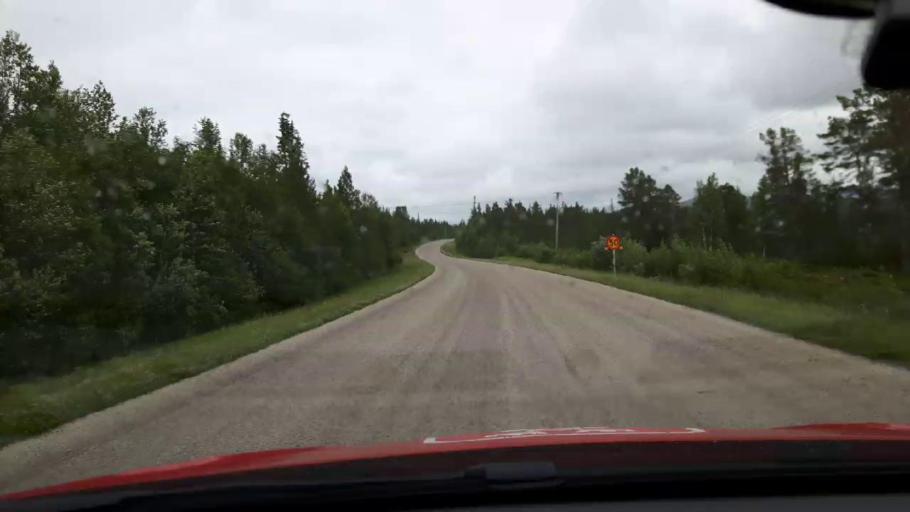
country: NO
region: Nord-Trondelag
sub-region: Meraker
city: Meraker
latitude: 63.2695
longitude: 12.3742
